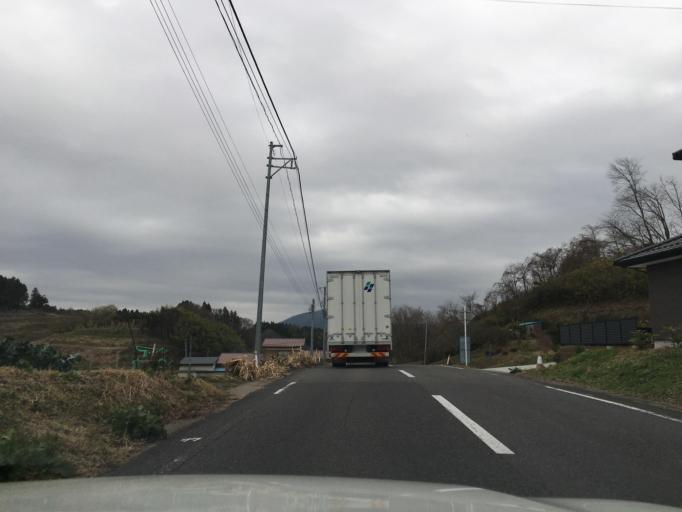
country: JP
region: Fukushima
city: Miharu
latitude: 37.4904
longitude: 140.5201
